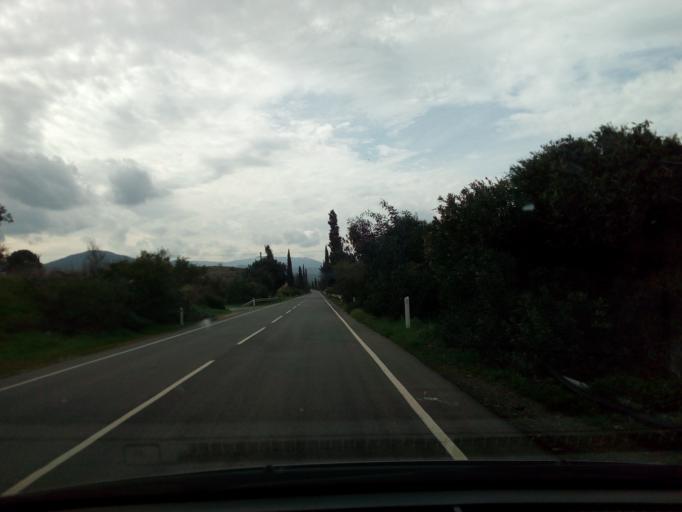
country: CY
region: Lefkosia
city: Astromeritis
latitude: 35.0976
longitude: 32.9688
